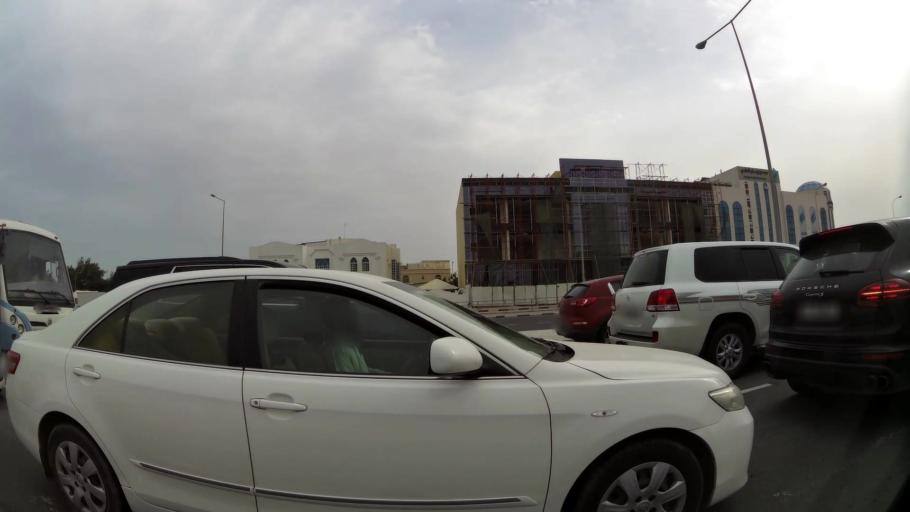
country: QA
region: Baladiyat ar Rayyan
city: Ar Rayyan
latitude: 25.3352
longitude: 51.4770
